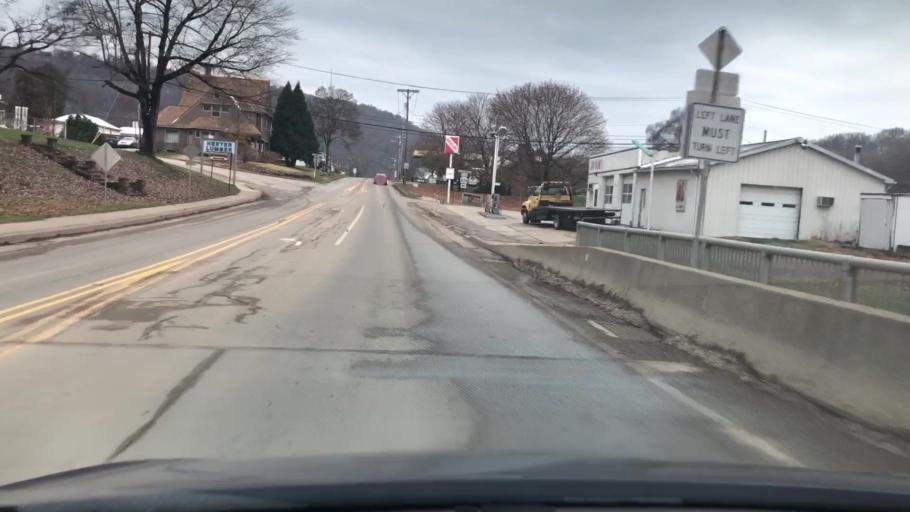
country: US
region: Pennsylvania
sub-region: Clarion County
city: Clarion
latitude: 41.0013
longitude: -79.3365
